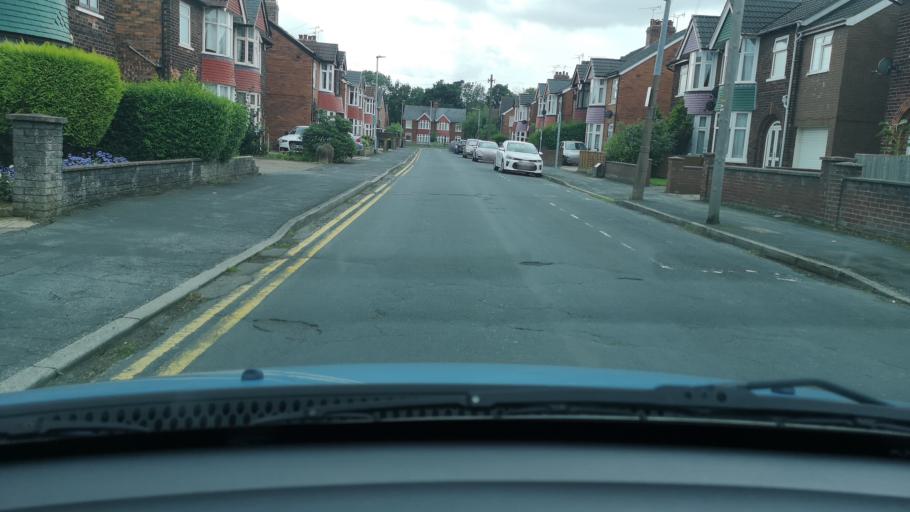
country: GB
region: England
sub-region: North Lincolnshire
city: Scunthorpe
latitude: 53.5872
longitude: -0.6644
